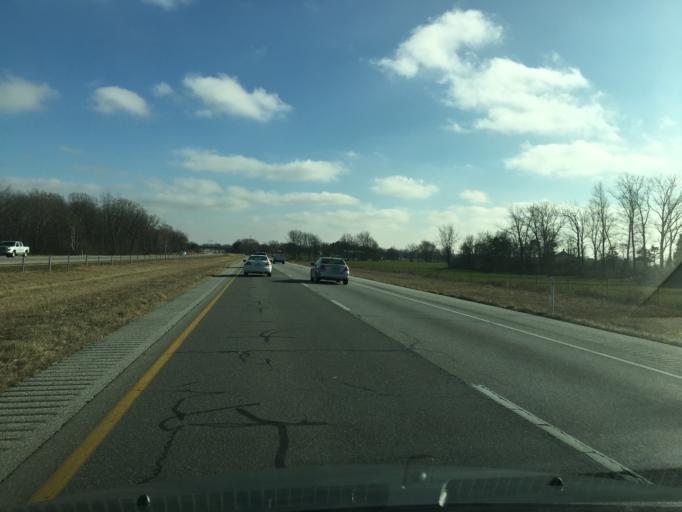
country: US
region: Indiana
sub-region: Decatur County
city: Saint Paul
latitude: 39.4811
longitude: -85.6748
